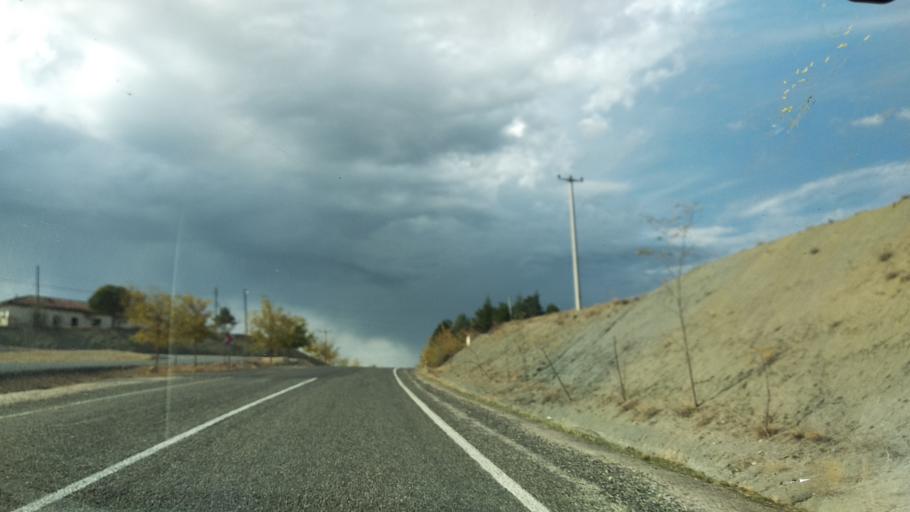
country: TR
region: Bolu
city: Seben
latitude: 40.3778
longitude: 31.5209
